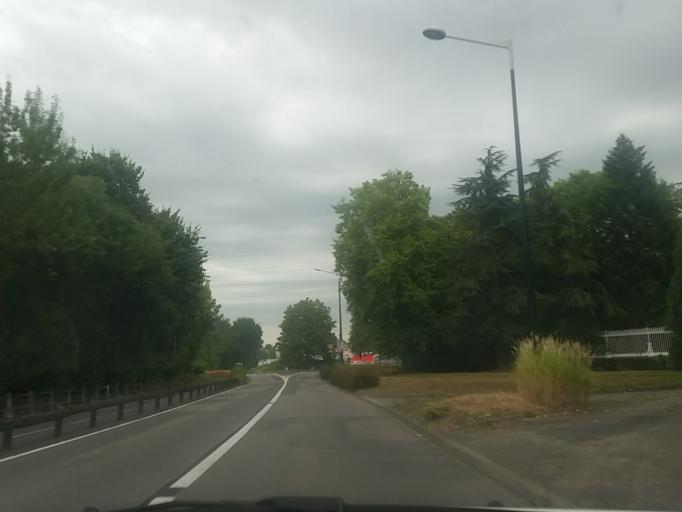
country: FR
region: Pays de la Loire
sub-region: Departement de la Loire-Atlantique
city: Saint-Sebastien-sur-Loire
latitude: 47.2113
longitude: -1.4925
